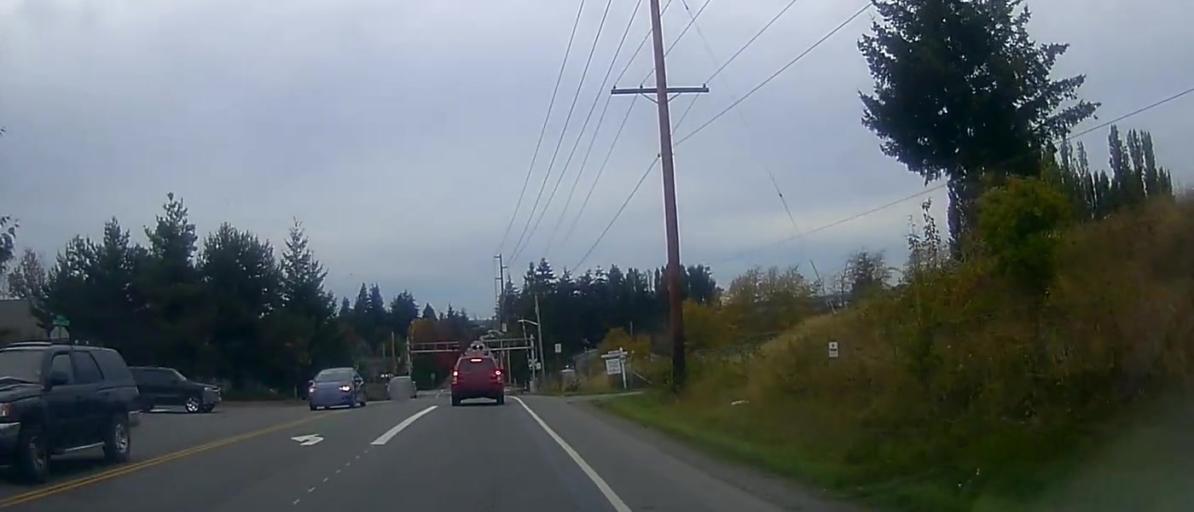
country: US
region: Washington
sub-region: Skagit County
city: Mount Vernon
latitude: 48.4430
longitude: -122.3240
